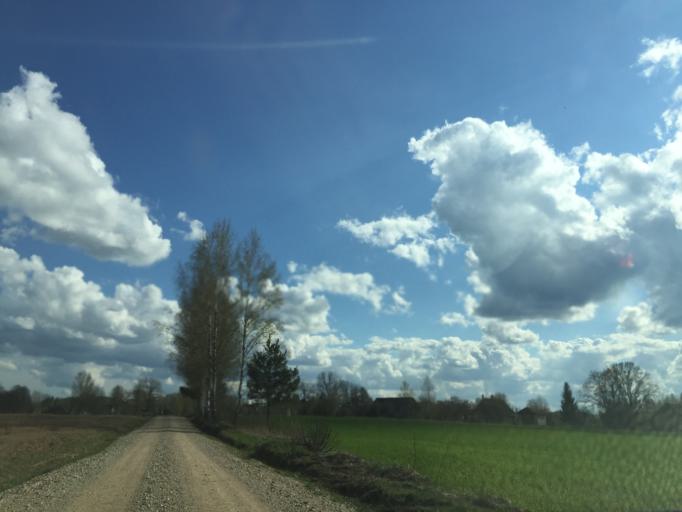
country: LV
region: Beverina
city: Murmuiza
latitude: 57.4229
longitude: 25.5496
